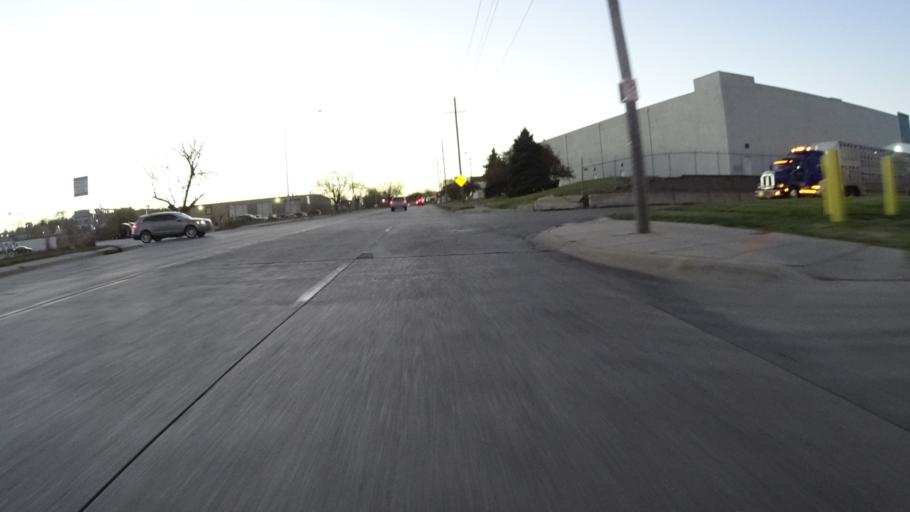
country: US
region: Nebraska
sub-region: Douglas County
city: Omaha
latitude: 41.2104
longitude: -95.9605
